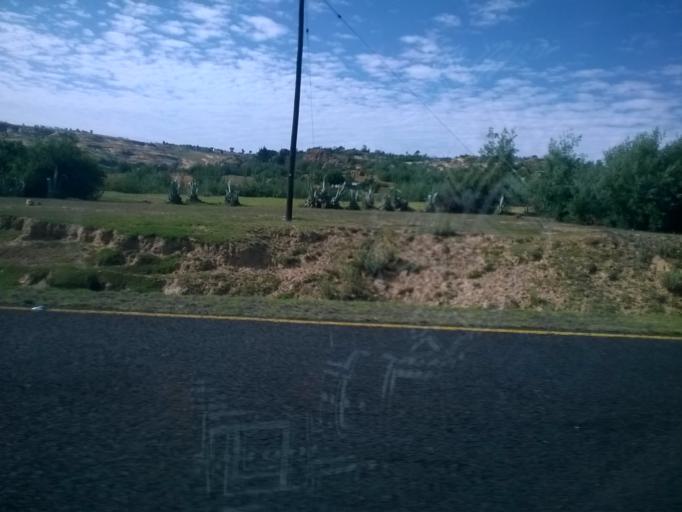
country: LS
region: Berea
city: Teyateyaneng
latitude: -29.1078
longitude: 27.8259
